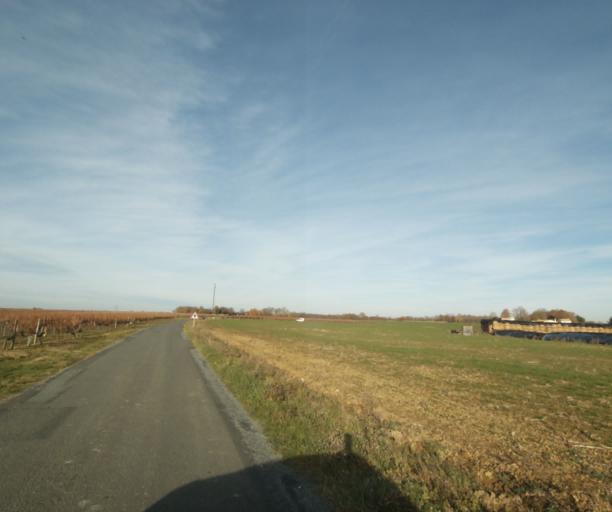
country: FR
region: Poitou-Charentes
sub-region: Departement de la Charente-Maritime
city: Chaniers
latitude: 45.7396
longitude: -0.5213
